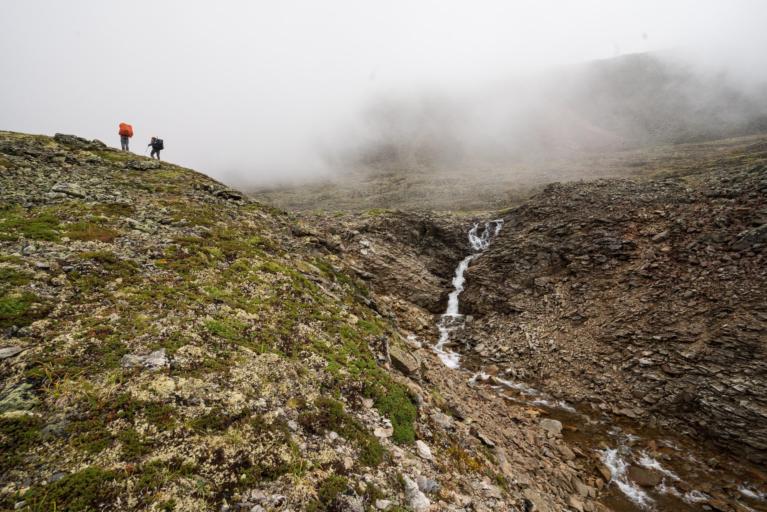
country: RU
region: Transbaikal Territory
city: Chara
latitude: 56.8683
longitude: 117.6532
